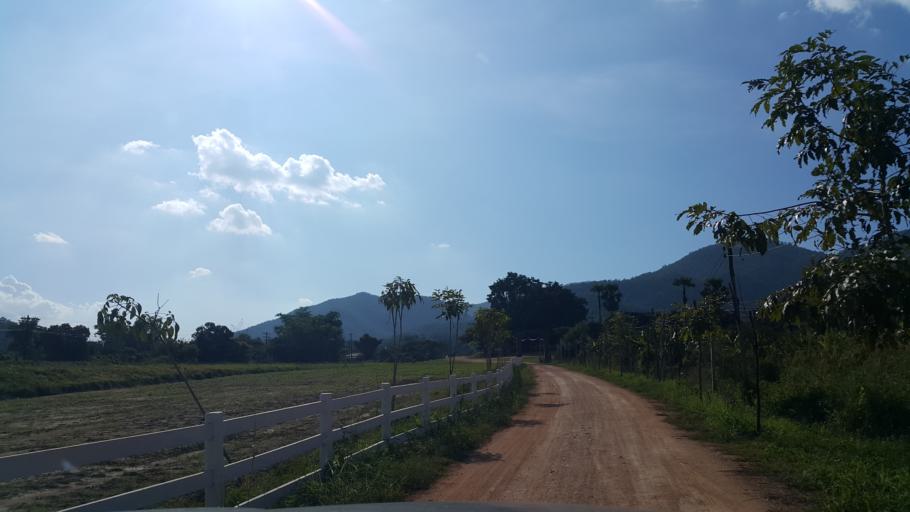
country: TH
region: Lamphun
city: Mae Tha
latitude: 18.5116
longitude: 99.2161
